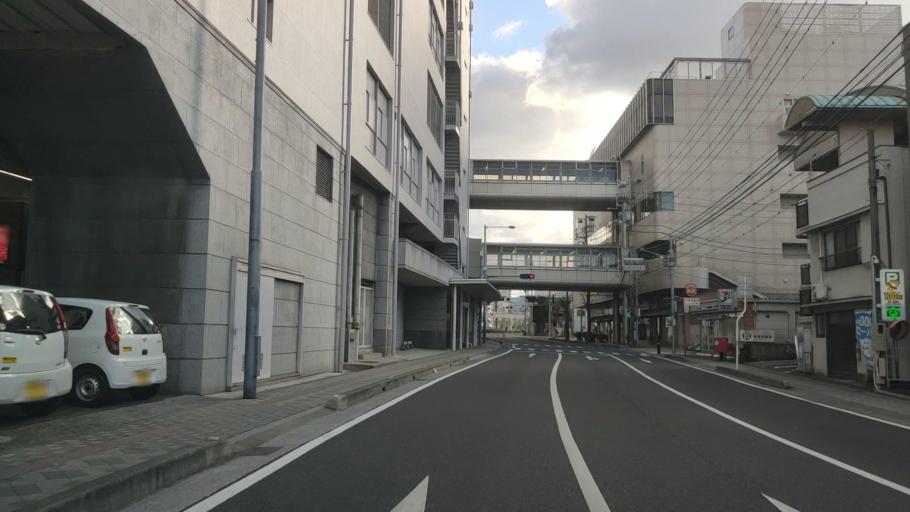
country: JP
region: Ehime
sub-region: Shikoku-chuo Shi
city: Matsuyama
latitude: 33.8354
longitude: 132.7618
